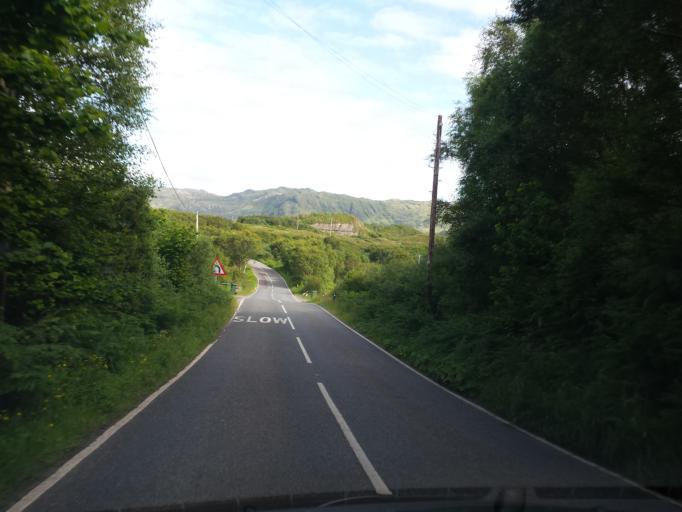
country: GB
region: Scotland
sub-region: Argyll and Bute
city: Isle Of Mull
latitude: 56.9623
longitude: -5.8284
